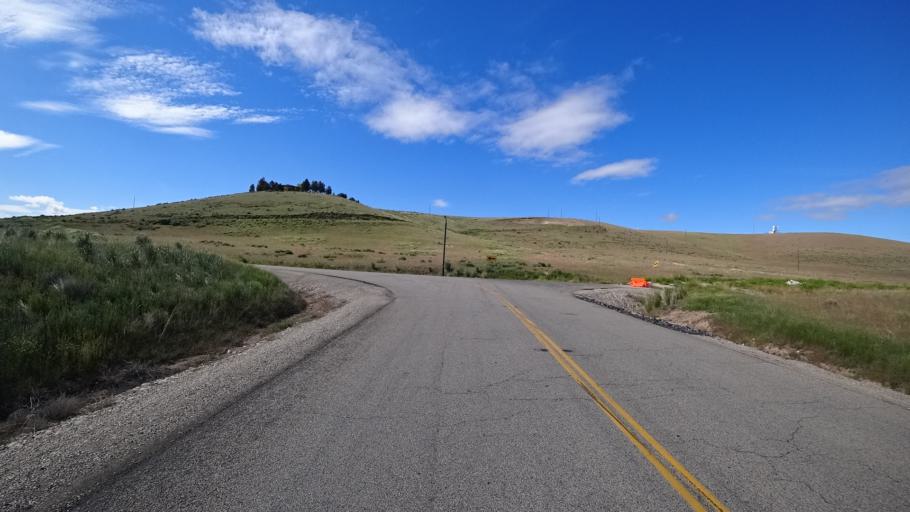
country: US
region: Idaho
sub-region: Ada County
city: Boise
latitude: 43.5124
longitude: -116.1516
